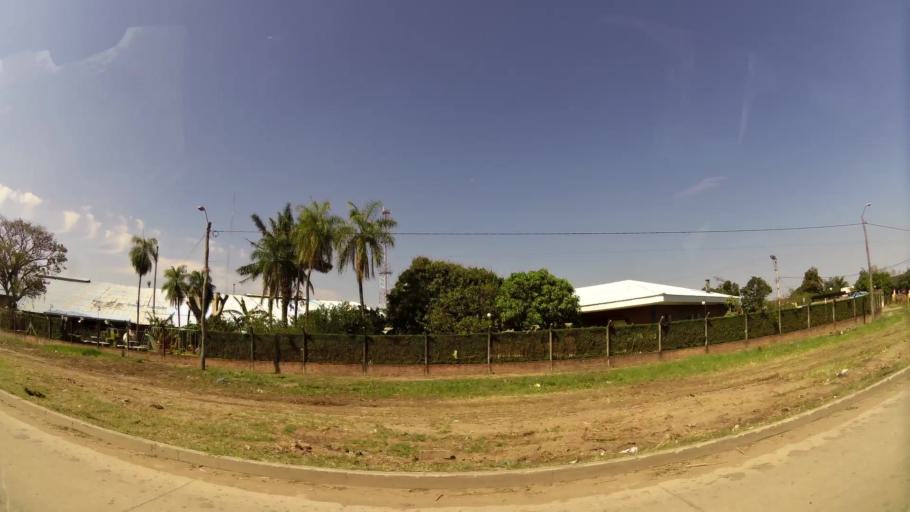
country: BO
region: Santa Cruz
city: Santa Cruz de la Sierra
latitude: -17.7572
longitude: -63.1205
